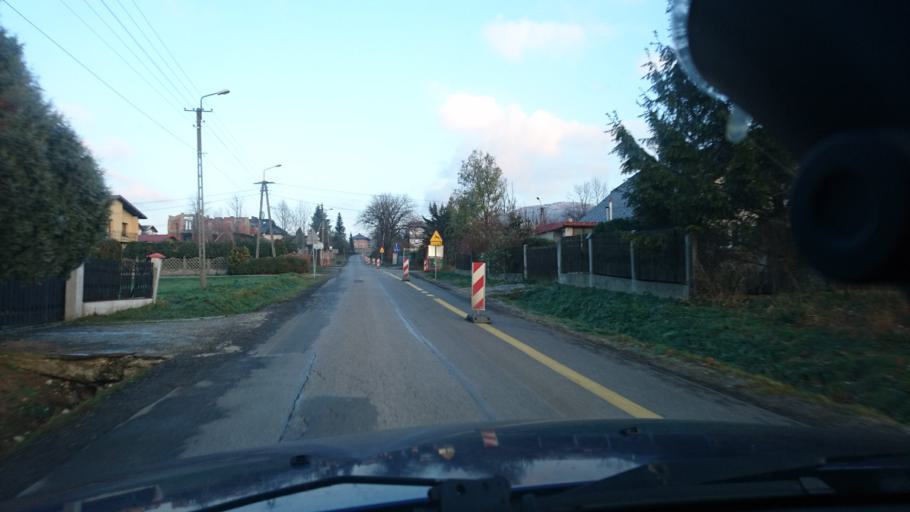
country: PL
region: Silesian Voivodeship
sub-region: Bielsko-Biala
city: Bielsko-Biala
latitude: 49.8207
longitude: 19.1004
